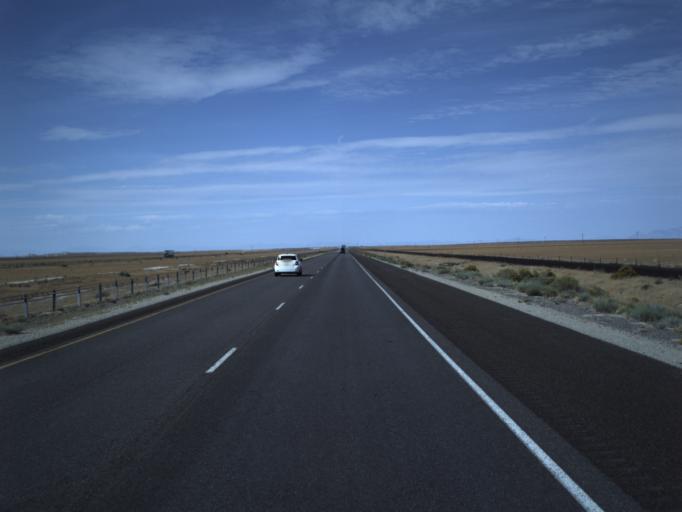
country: US
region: Utah
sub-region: Tooele County
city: Grantsville
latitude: 40.7269
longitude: -113.2180
